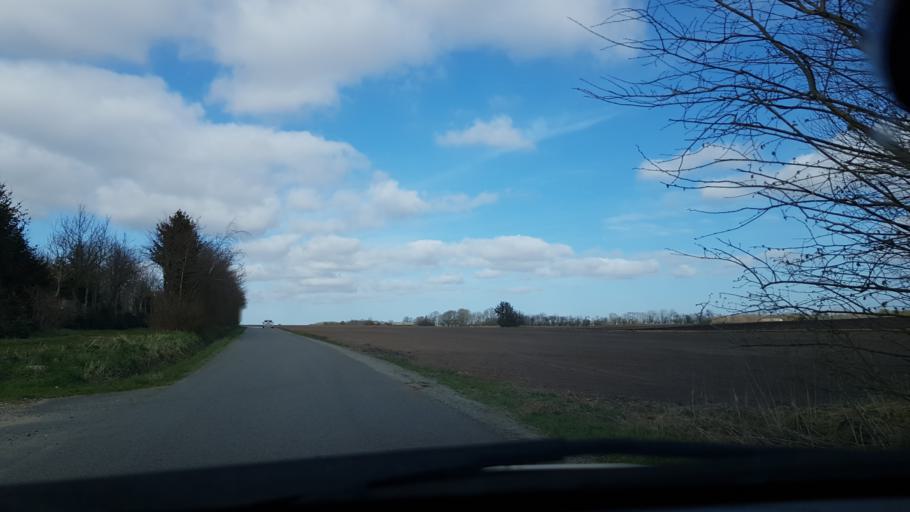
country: DK
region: South Denmark
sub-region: Vejen Kommune
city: Rodding
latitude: 55.3891
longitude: 9.0053
